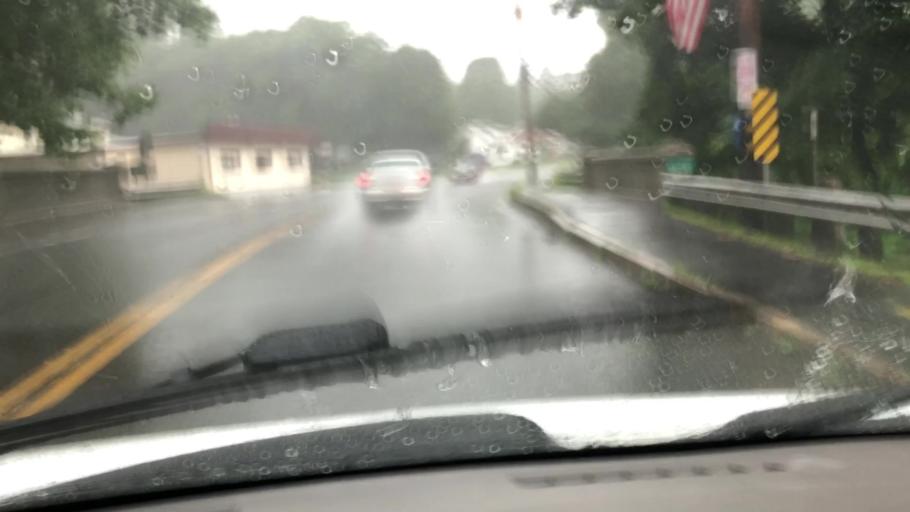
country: US
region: Massachusetts
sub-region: Berkshire County
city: Lanesborough
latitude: 42.5587
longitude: -73.1674
